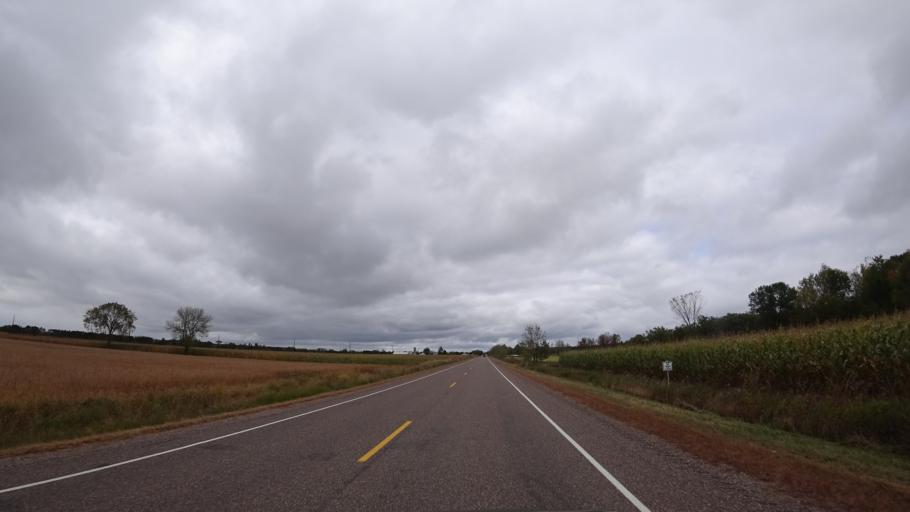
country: US
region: Wisconsin
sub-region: Chippewa County
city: Lake Wissota
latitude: 45.0014
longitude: -91.2867
